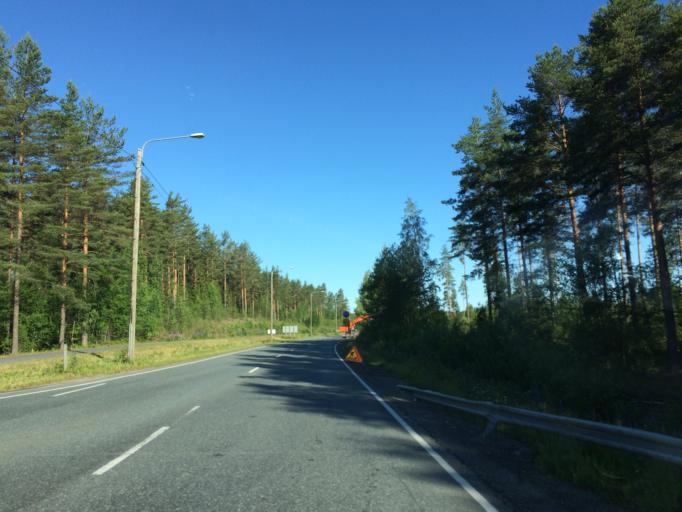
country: FI
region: Haeme
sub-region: Haemeenlinna
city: Haemeenlinna
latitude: 60.9606
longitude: 24.4564
